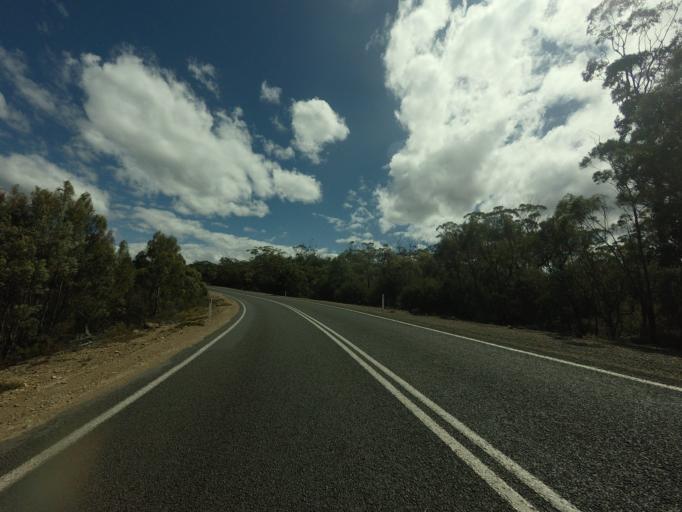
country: AU
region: Tasmania
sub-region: Break O'Day
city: St Helens
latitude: -42.0140
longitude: 147.9603
